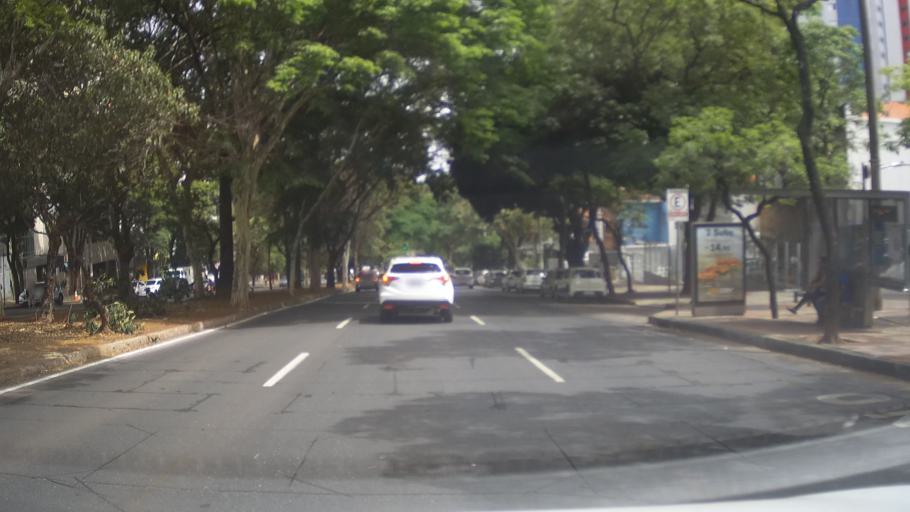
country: BR
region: Minas Gerais
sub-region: Belo Horizonte
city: Belo Horizonte
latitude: -19.9374
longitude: -43.9272
